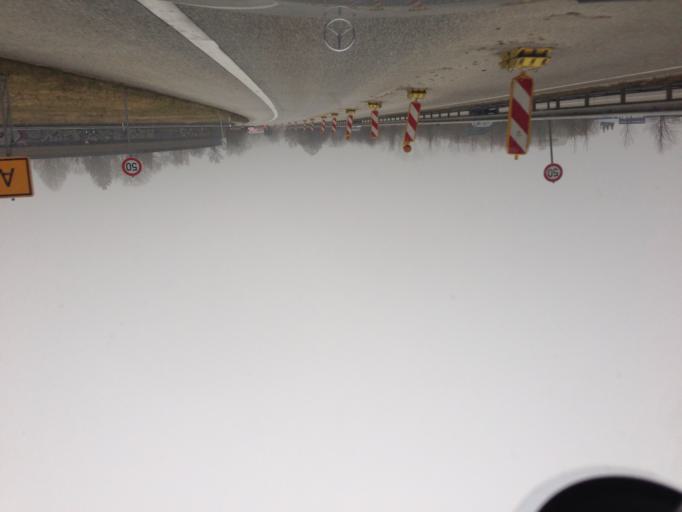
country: DE
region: Schleswig-Holstein
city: Klein Barkau
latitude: 54.2763
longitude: 10.1426
